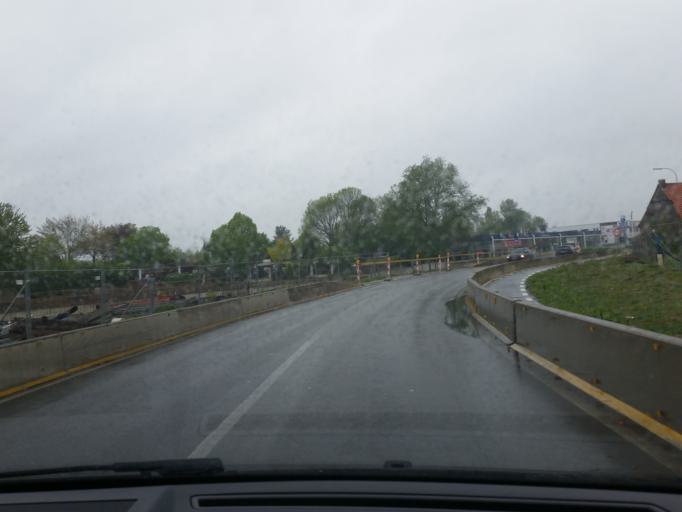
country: BE
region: Flanders
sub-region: Provincie Antwerpen
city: Borsbeek
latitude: 51.1901
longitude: 4.4761
